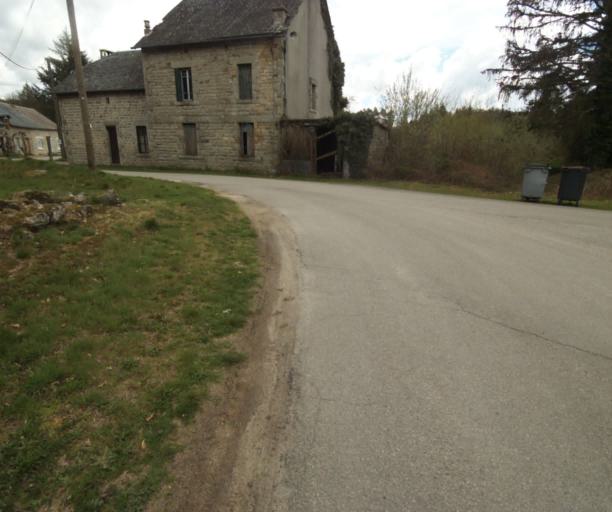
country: FR
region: Limousin
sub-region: Departement de la Correze
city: Correze
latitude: 45.3277
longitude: 1.9381
